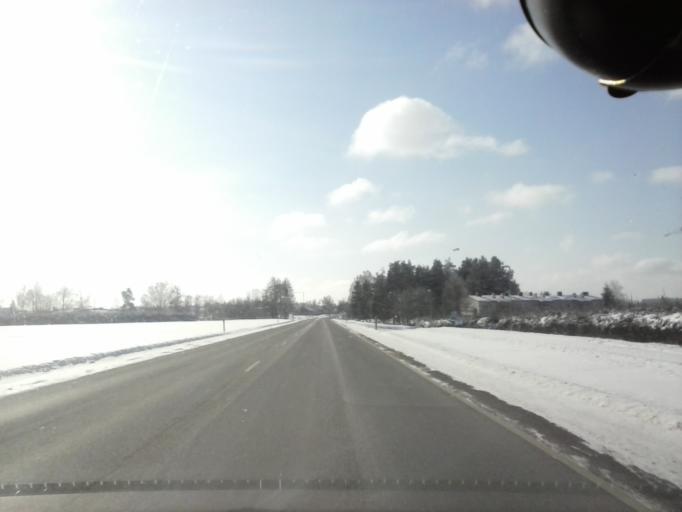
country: EE
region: Viljandimaa
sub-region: Viiratsi vald
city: Viiratsi
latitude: 58.3704
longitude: 25.6482
